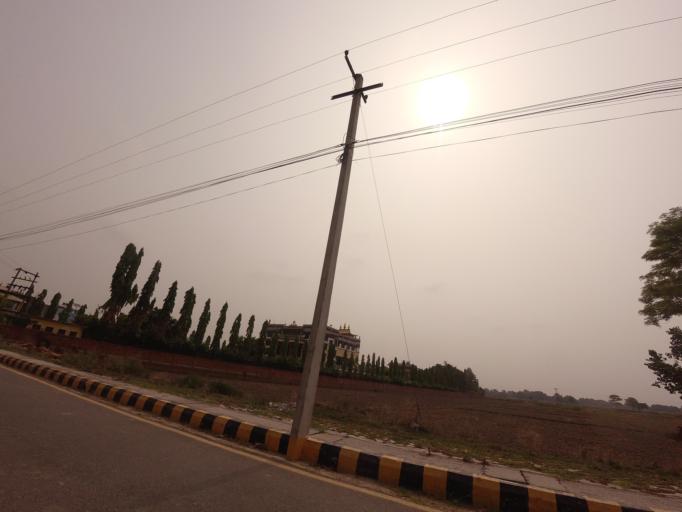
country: IN
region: Uttar Pradesh
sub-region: Maharajganj
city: Nautanwa
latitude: 27.4654
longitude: 83.2838
